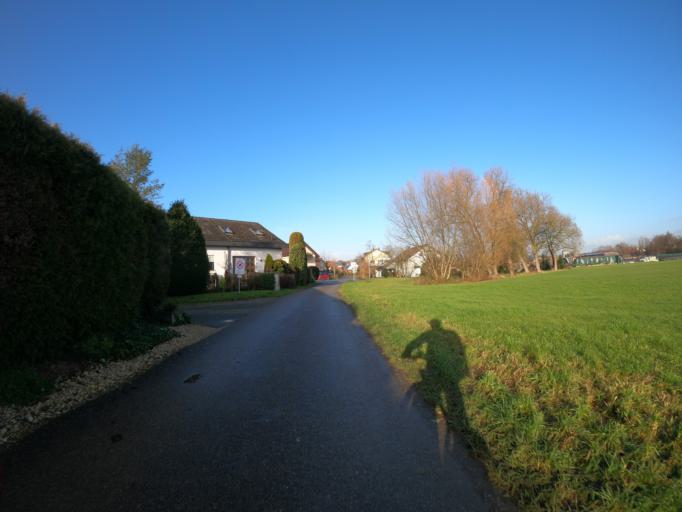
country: DE
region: Baden-Wuerttemberg
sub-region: Regierungsbezirk Stuttgart
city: Hattenhofen
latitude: 48.6640
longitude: 9.5777
